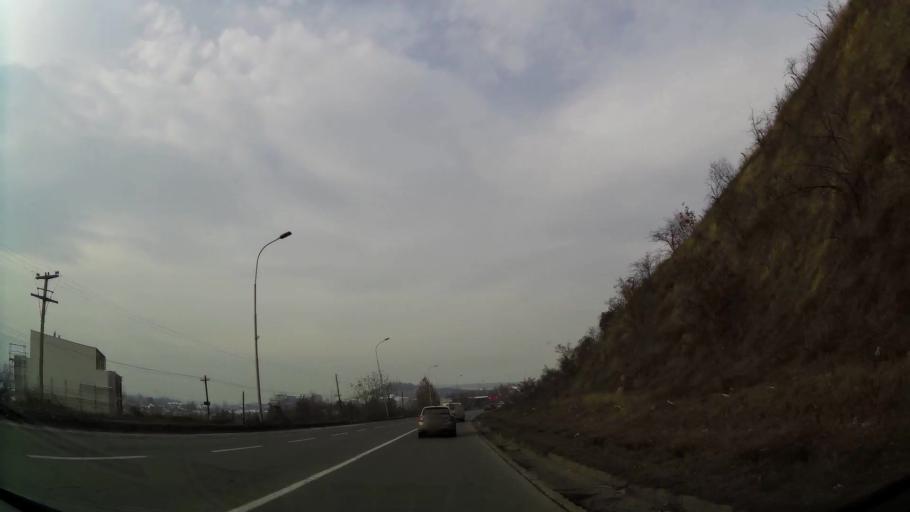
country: MK
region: Karpos
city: Skopje
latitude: 42.0143
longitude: 21.4151
